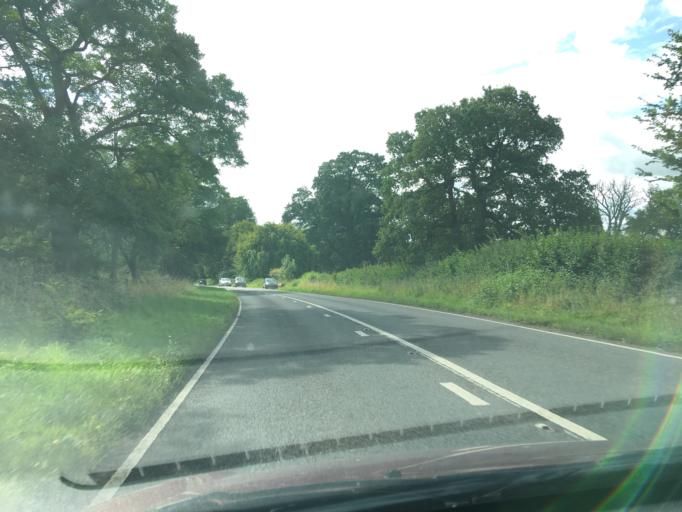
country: GB
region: England
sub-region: Warwickshire
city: Royal Leamington Spa
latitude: 52.3429
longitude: -1.5166
